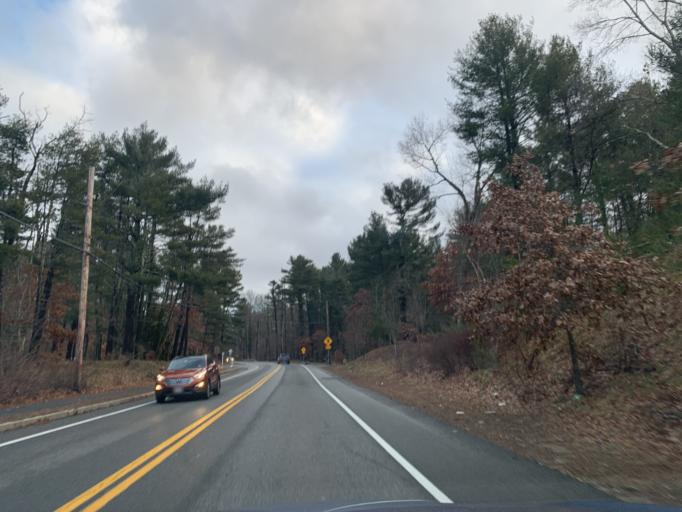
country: US
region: Massachusetts
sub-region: Norfolk County
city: Wrentham
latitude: 42.0877
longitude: -71.2941
